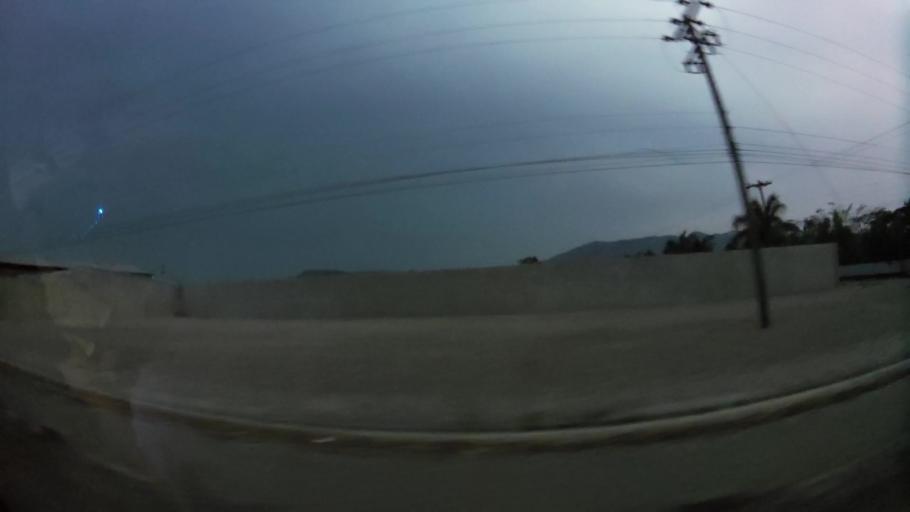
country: NI
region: Esteli
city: Esteli
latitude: 13.1064
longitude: -86.3592
